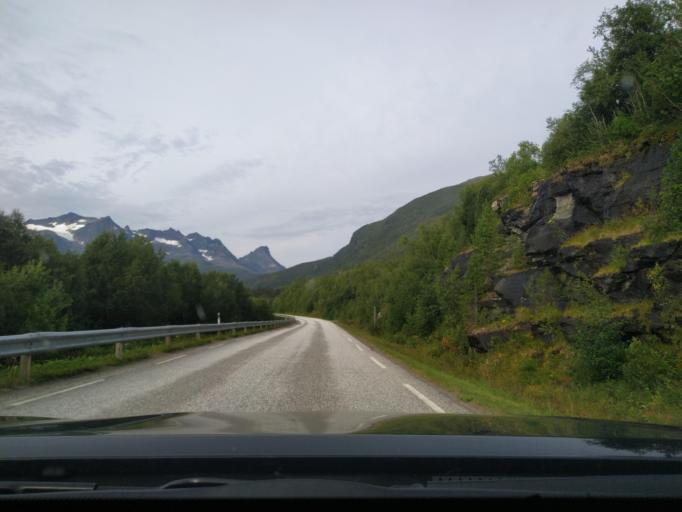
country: NO
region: Troms
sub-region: Dyroy
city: Brostadbotn
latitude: 68.9113
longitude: 17.5405
